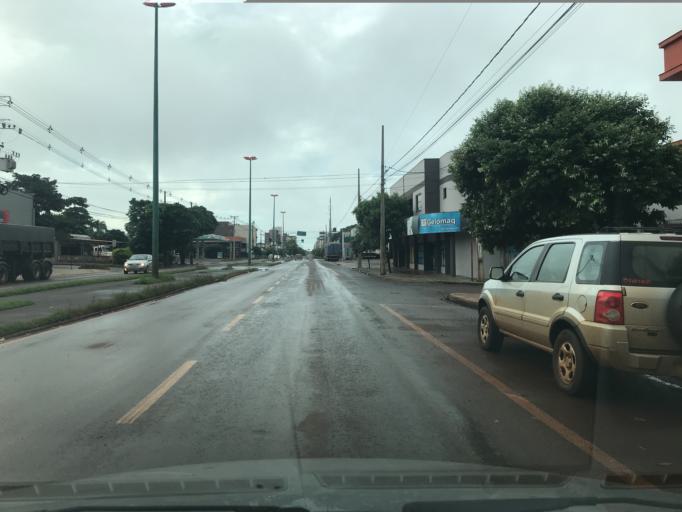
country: BR
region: Parana
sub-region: Palotina
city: Palotina
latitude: -24.2911
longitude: -53.8374
